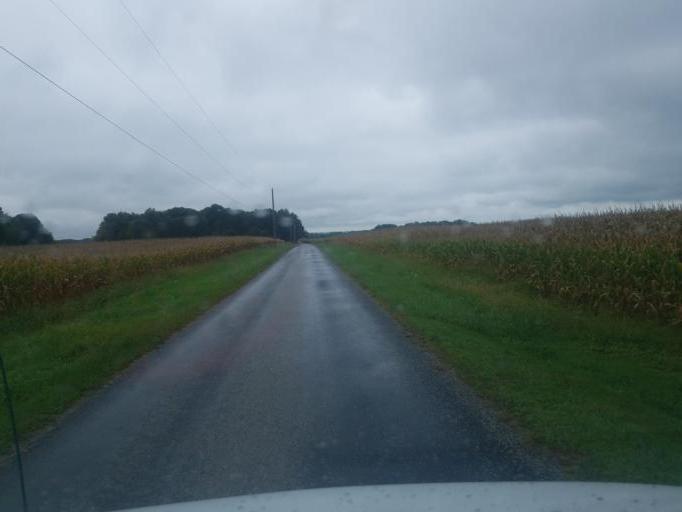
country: US
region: Ohio
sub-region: Ashland County
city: Ashland
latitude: 40.8426
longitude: -82.1801
